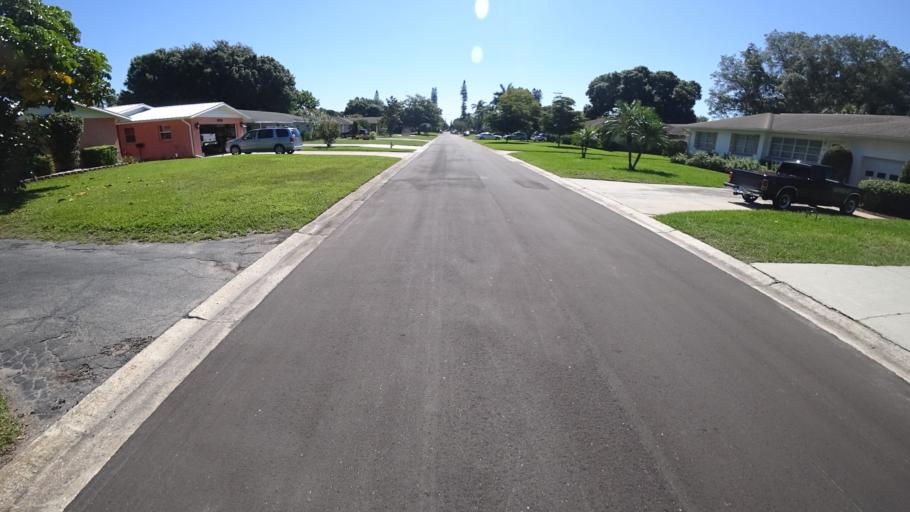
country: US
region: Florida
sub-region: Manatee County
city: West Bradenton
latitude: 27.4857
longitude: -82.6012
